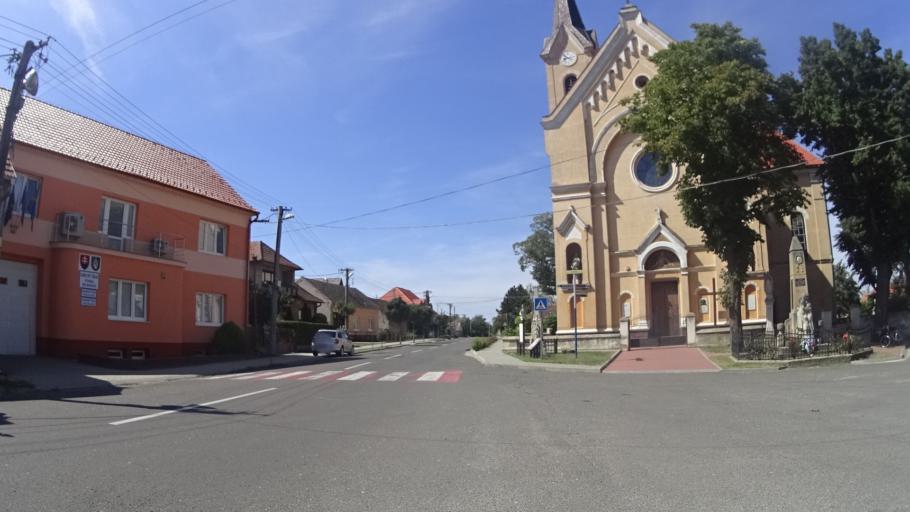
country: AT
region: Lower Austria
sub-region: Politischer Bezirk Ganserndorf
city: Marchegg
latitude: 48.3302
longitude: 16.9078
